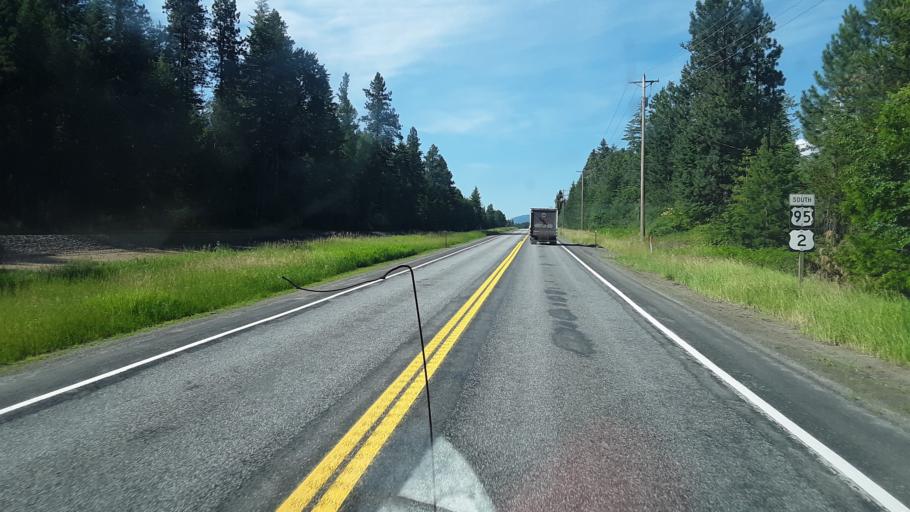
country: US
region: Idaho
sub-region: Bonner County
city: Ponderay
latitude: 48.5003
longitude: -116.4494
